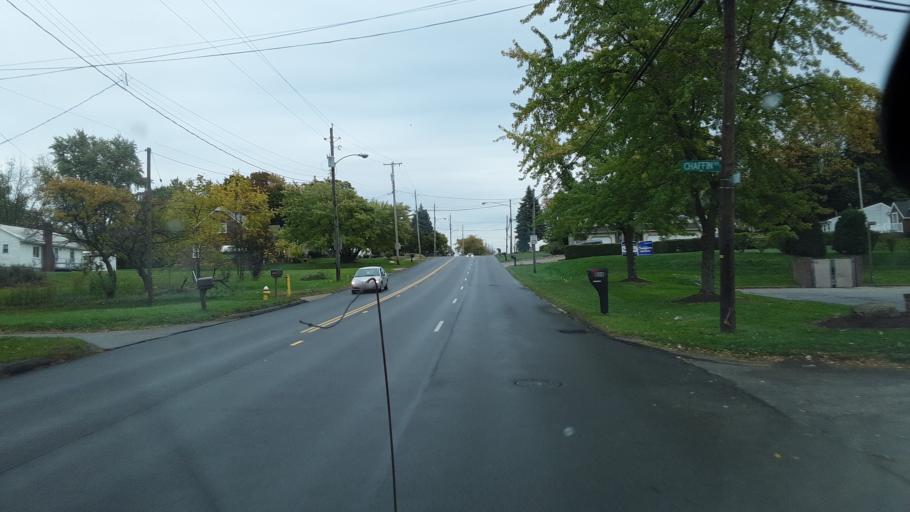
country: US
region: Ohio
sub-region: Summit County
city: Portage Lakes
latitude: 41.0295
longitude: -81.4991
